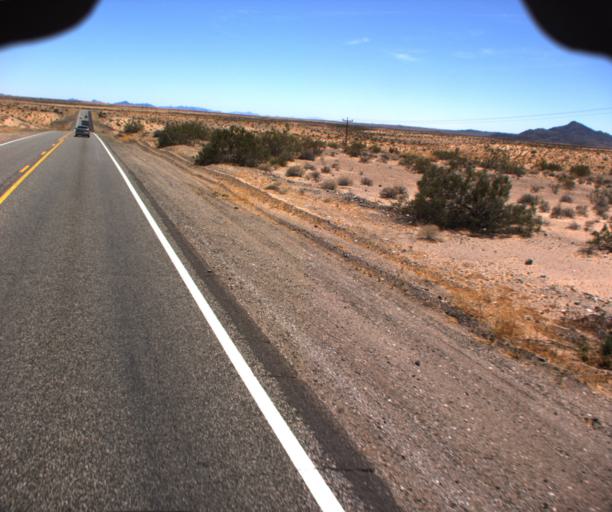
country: US
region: Arizona
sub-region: La Paz County
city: Parker
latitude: 34.0773
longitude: -114.2649
